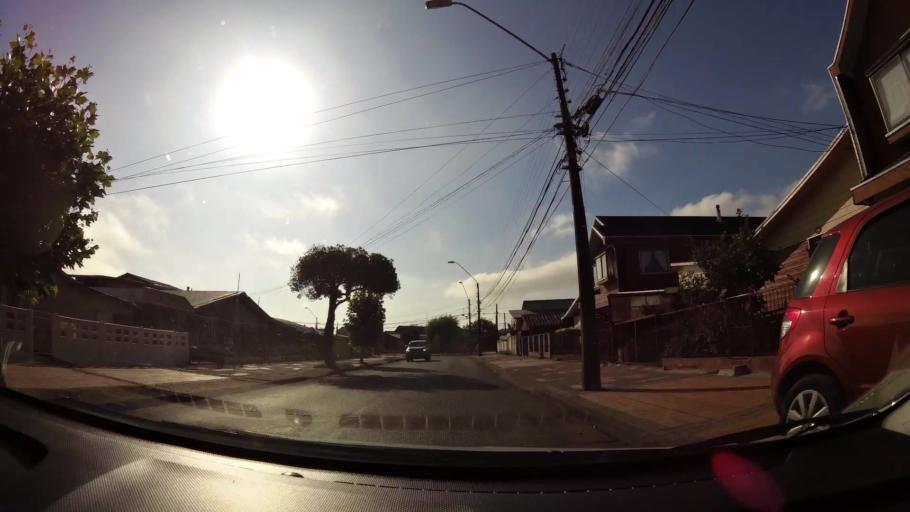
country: CL
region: Biobio
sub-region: Provincia de Concepcion
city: Concepcion
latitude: -36.7938
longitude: -73.1059
